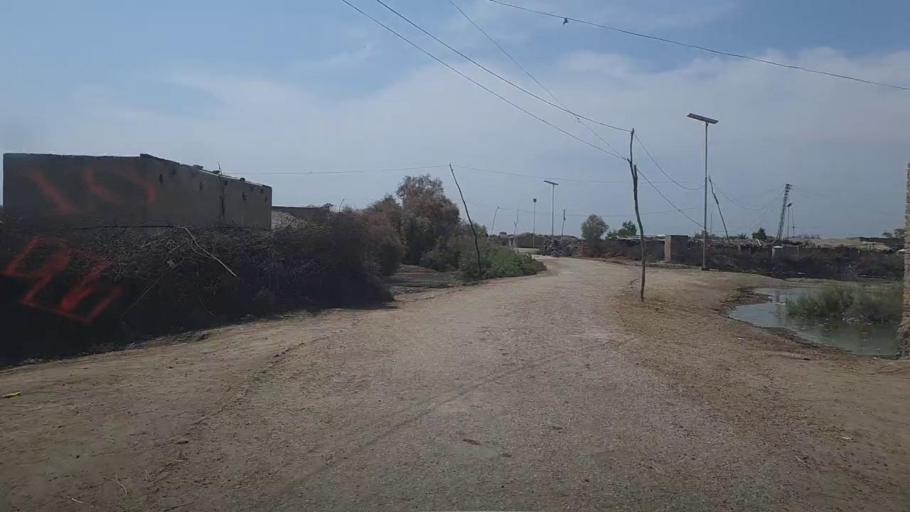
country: PK
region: Sindh
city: Kandhkot
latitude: 28.3109
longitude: 69.2266
